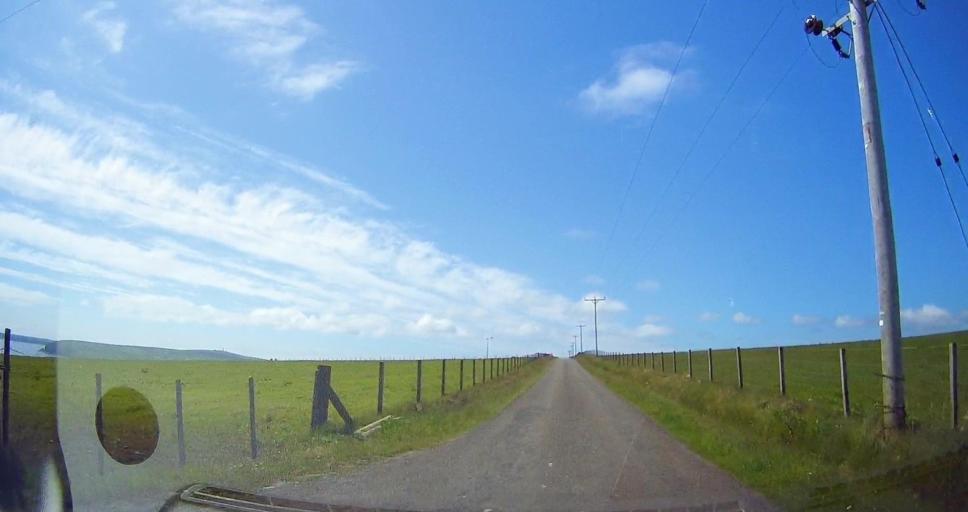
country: GB
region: Scotland
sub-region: Orkney Islands
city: Kirkwall
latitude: 58.8159
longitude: -2.9155
